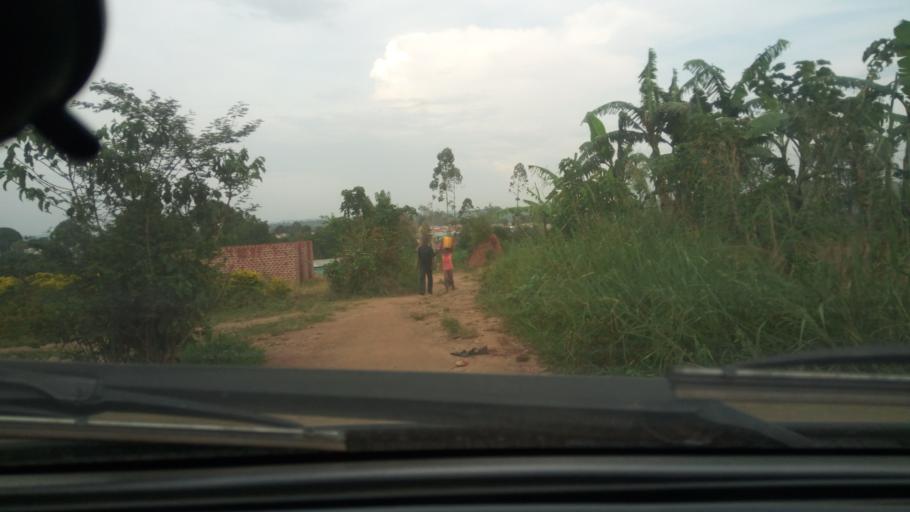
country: UG
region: Central Region
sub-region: Mityana District
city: Mityana
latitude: 0.5663
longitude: 32.1973
